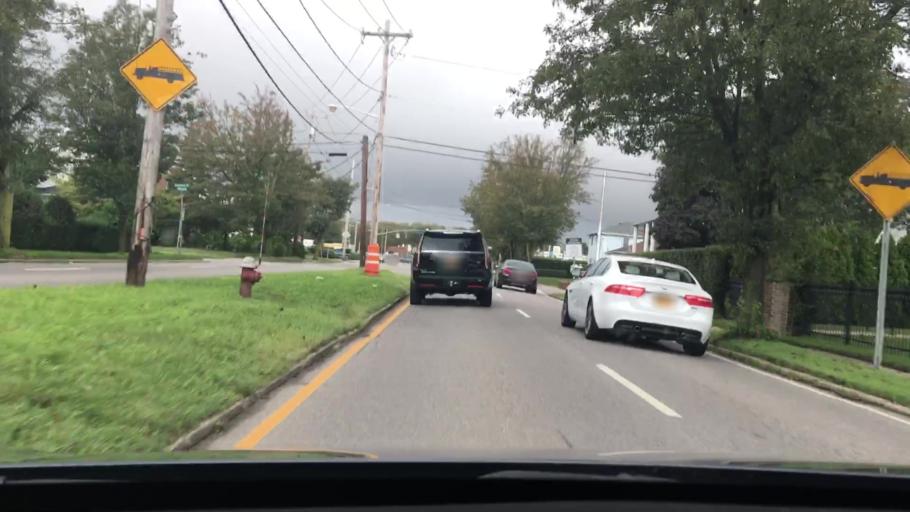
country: US
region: New York
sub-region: Nassau County
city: Garden City Park
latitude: 40.7396
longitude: -73.6623
